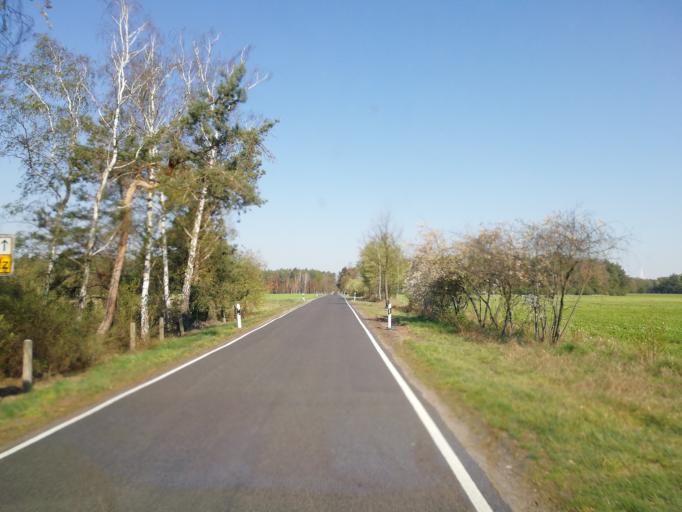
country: DE
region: Brandenburg
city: Bronkow
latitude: 51.7053
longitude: 13.8758
